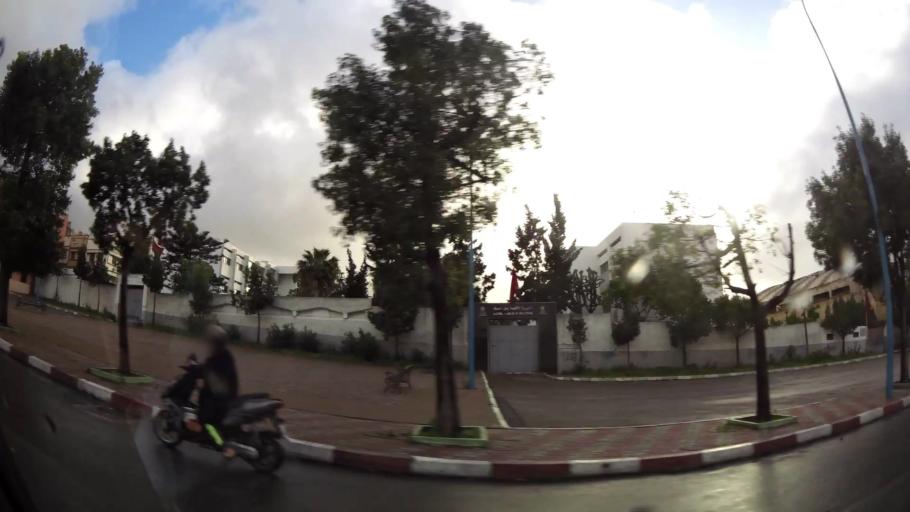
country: MA
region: Grand Casablanca
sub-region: Casablanca
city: Casablanca
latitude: 33.5593
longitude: -7.5748
